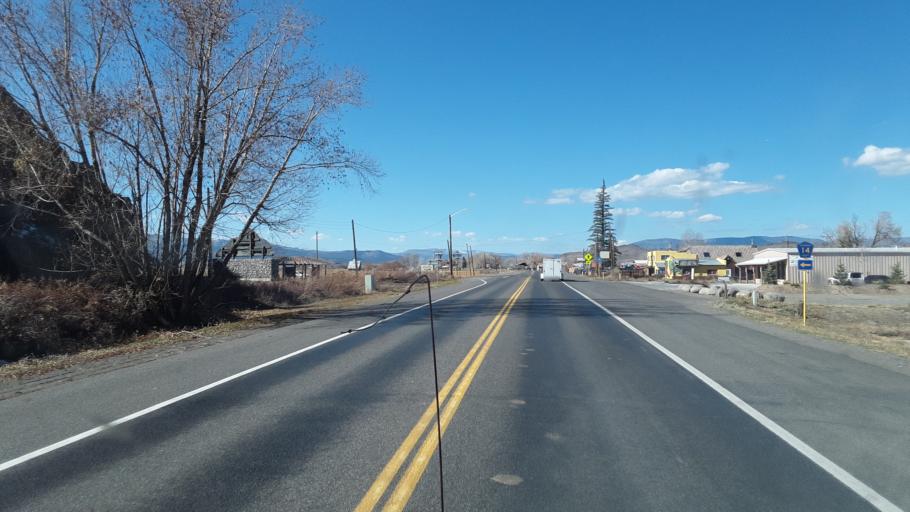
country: US
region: Colorado
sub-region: Rio Grande County
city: Del Norte
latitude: 37.6794
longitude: -106.3600
